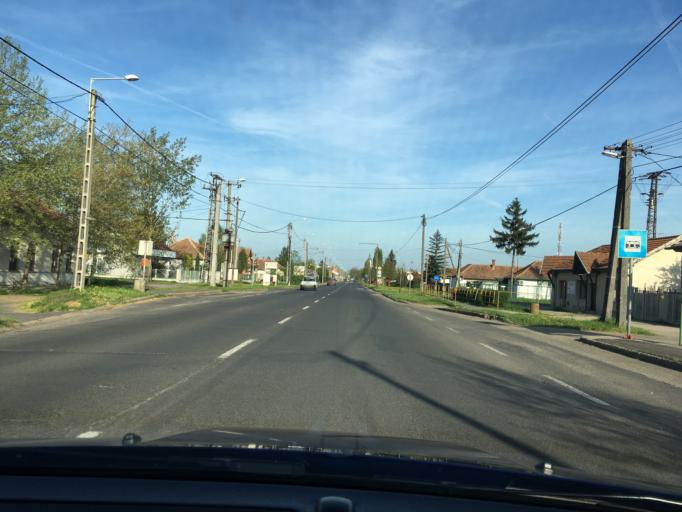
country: HU
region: Bekes
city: Szeghalom
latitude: 47.0166
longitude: 21.1625
